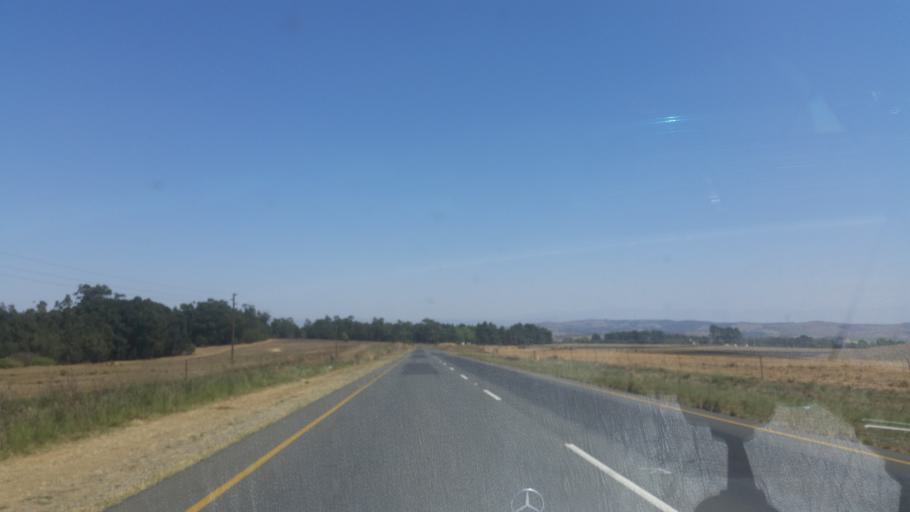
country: ZA
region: KwaZulu-Natal
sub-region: uMgungundlovu District Municipality
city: Mooirivier
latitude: -29.1461
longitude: 29.9896
